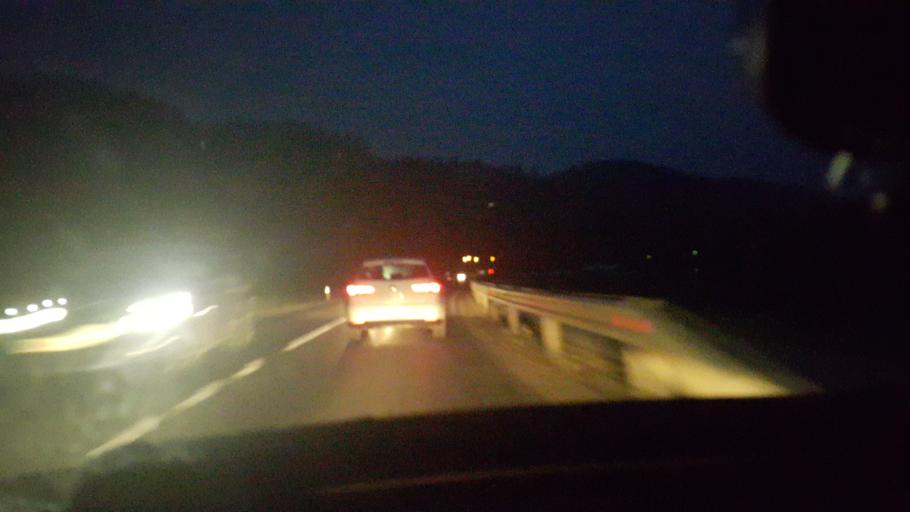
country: SI
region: Muta
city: Muta
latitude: 46.6136
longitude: 15.1740
